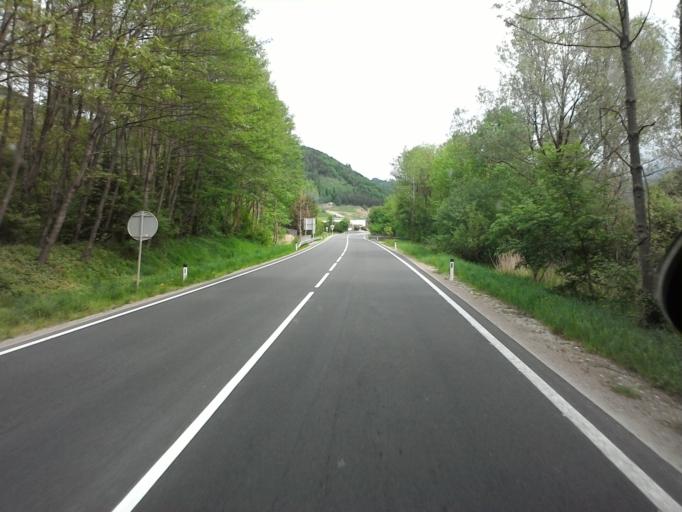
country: AT
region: Upper Austria
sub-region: Politischer Bezirk Kirchdorf an der Krems
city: Micheldorf in Oberoesterreich
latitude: 47.8696
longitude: 14.1383
